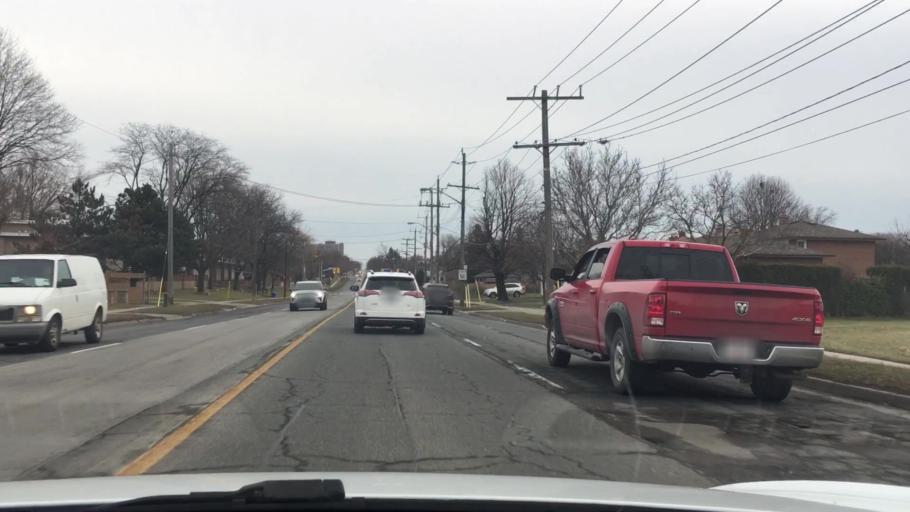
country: CA
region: Ontario
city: Scarborough
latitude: 43.7482
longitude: -79.2639
